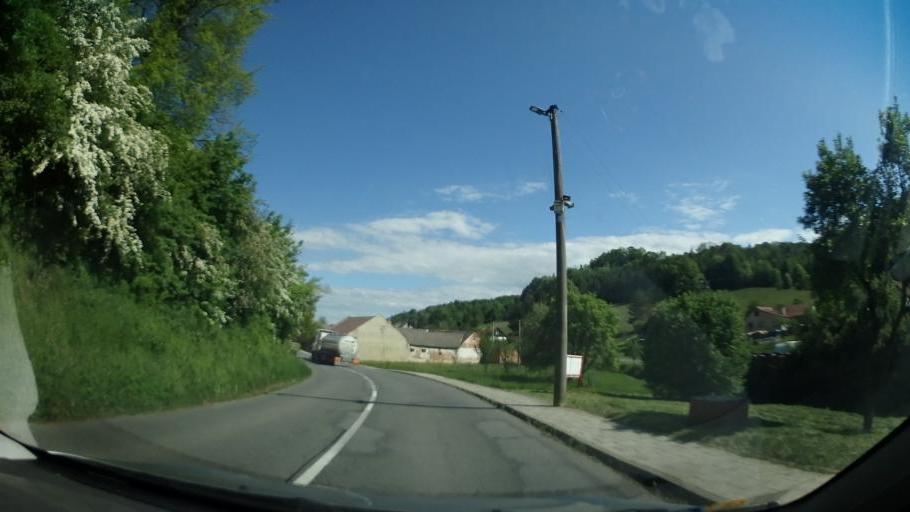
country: CZ
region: Pardubicky
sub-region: Okres Svitavy
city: Moravska Trebova
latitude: 49.7054
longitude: 16.6414
